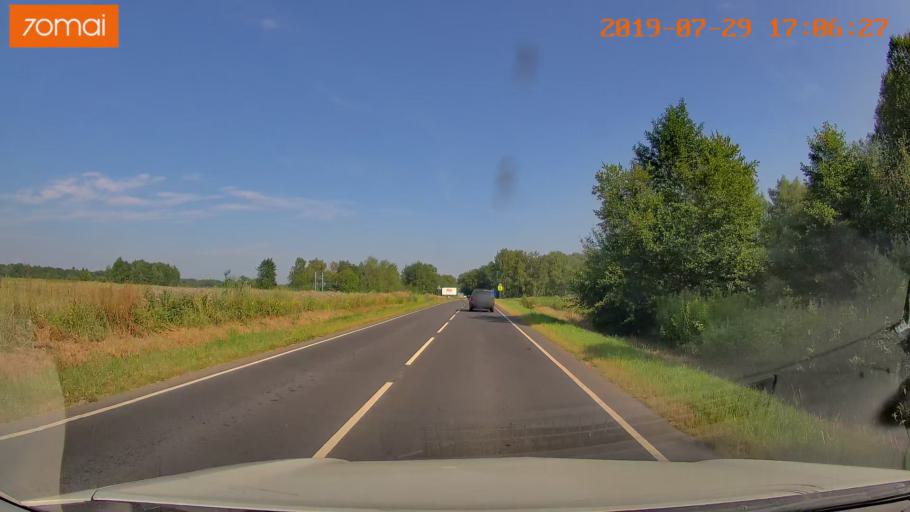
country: RU
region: Kaliningrad
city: Vzmorye
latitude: 54.8201
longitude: 20.3076
